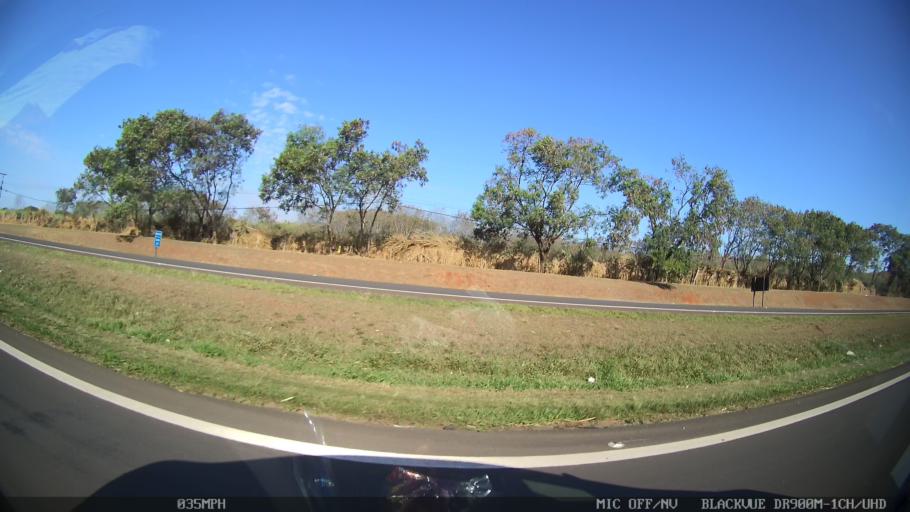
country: BR
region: Sao Paulo
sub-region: Piracicaba
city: Piracicaba
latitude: -22.6650
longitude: -47.6196
